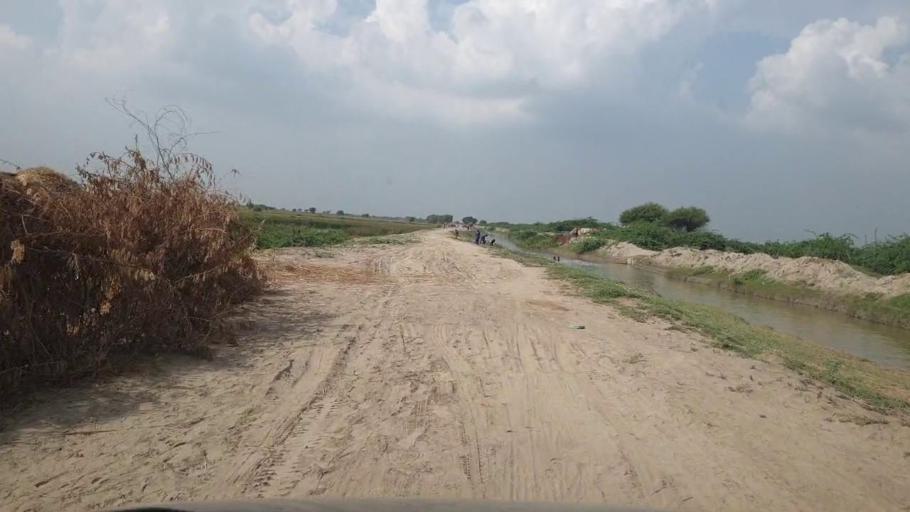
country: PK
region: Sindh
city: Badin
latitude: 24.5700
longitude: 68.6329
